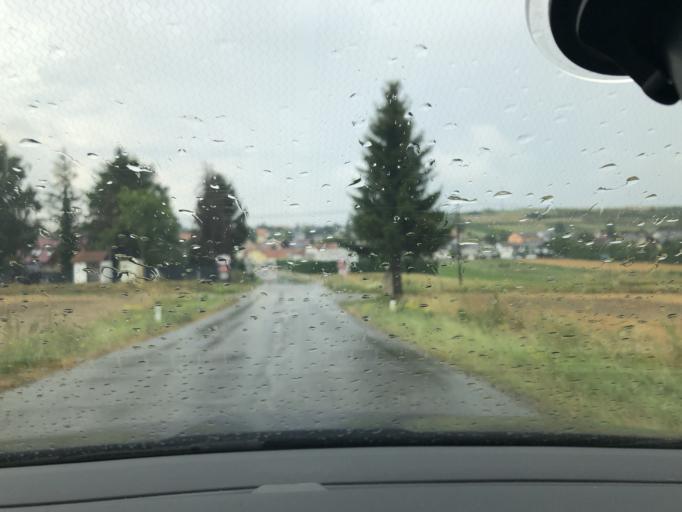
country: AT
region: Lower Austria
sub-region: Politischer Bezirk Ganserndorf
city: Auersthal
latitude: 48.3893
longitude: 16.6542
